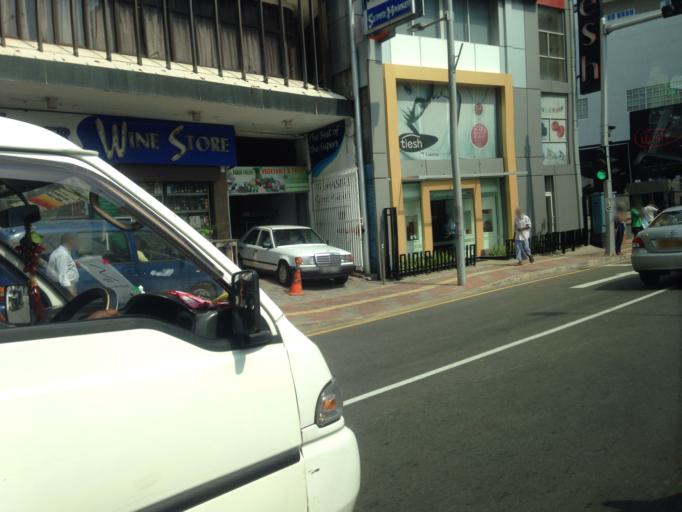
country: LK
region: Western
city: Colombo
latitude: 6.9107
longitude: 79.8520
